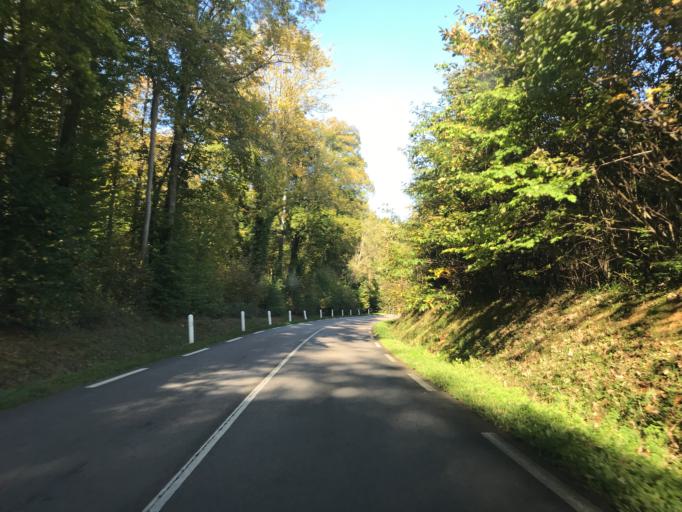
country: FR
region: Haute-Normandie
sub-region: Departement de l'Eure
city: Gravigny
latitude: 49.0786
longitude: 1.2496
